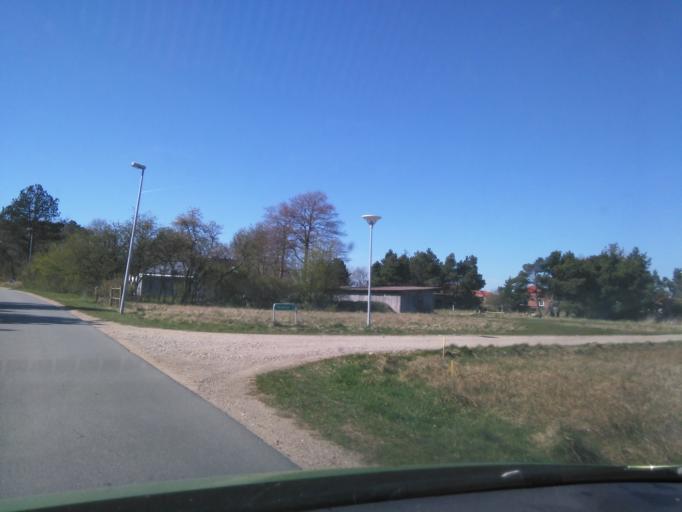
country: DK
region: South Denmark
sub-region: Varde Kommune
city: Oksbol
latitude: 55.5489
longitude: 8.2260
